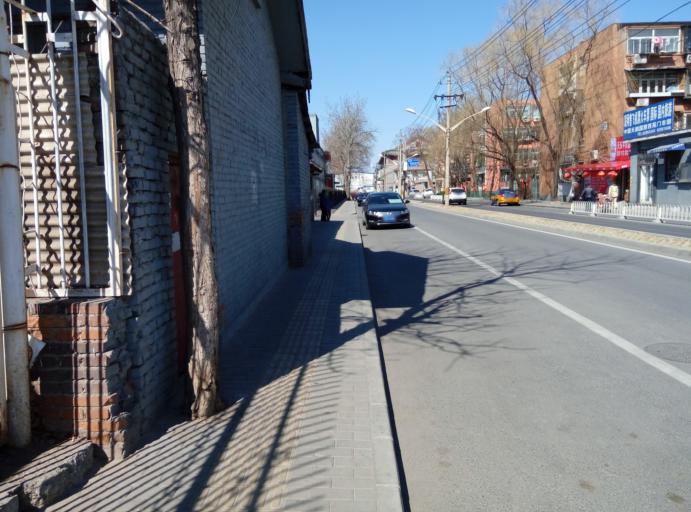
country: CN
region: Beijing
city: Haidian
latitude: 39.9909
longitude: 116.2864
